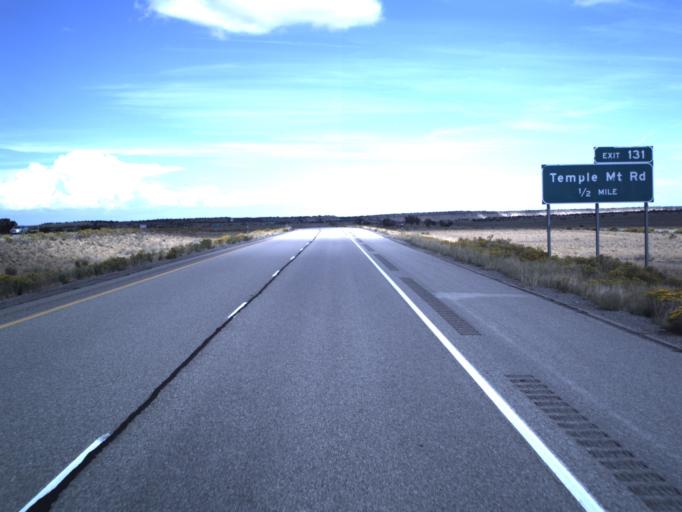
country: US
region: Utah
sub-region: Emery County
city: Castle Dale
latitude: 38.8755
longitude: -110.6702
